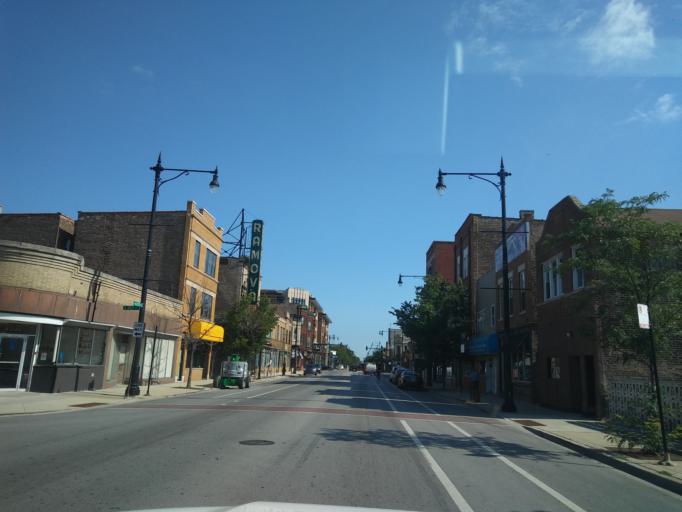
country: US
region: Illinois
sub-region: Cook County
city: Chicago
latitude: 41.8296
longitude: -87.6461
